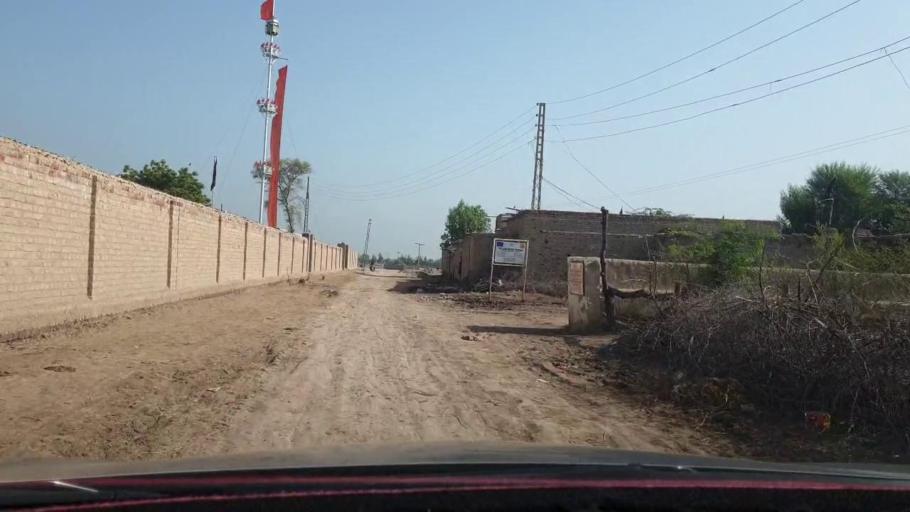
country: PK
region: Sindh
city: Nasirabad
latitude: 27.4536
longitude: 67.9173
